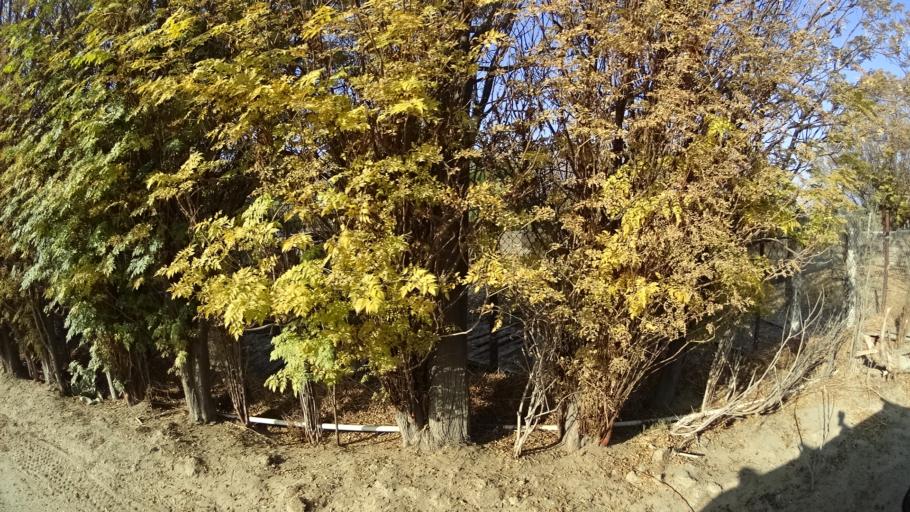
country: US
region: California
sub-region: Kern County
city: Greenfield
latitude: 35.2632
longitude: -119.0302
